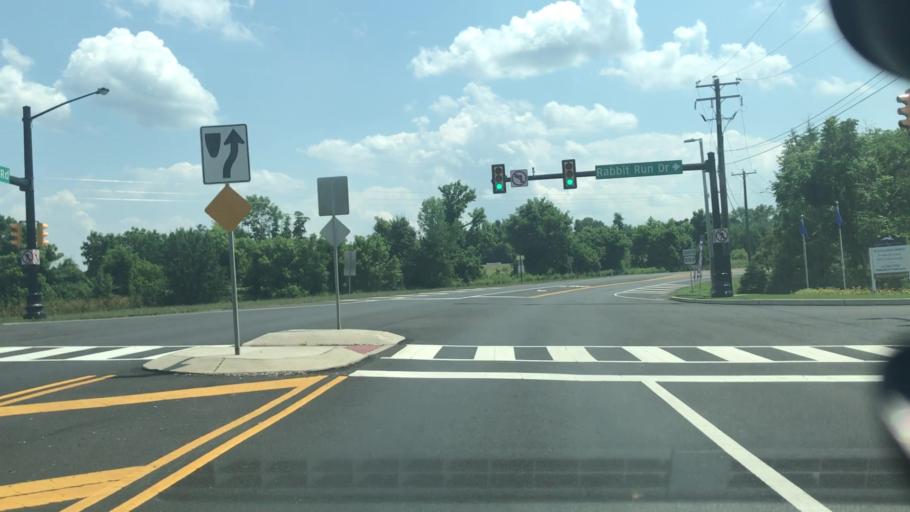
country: US
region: Pennsylvania
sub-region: Bucks County
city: New Hope
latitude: 40.3716
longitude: -74.9630
